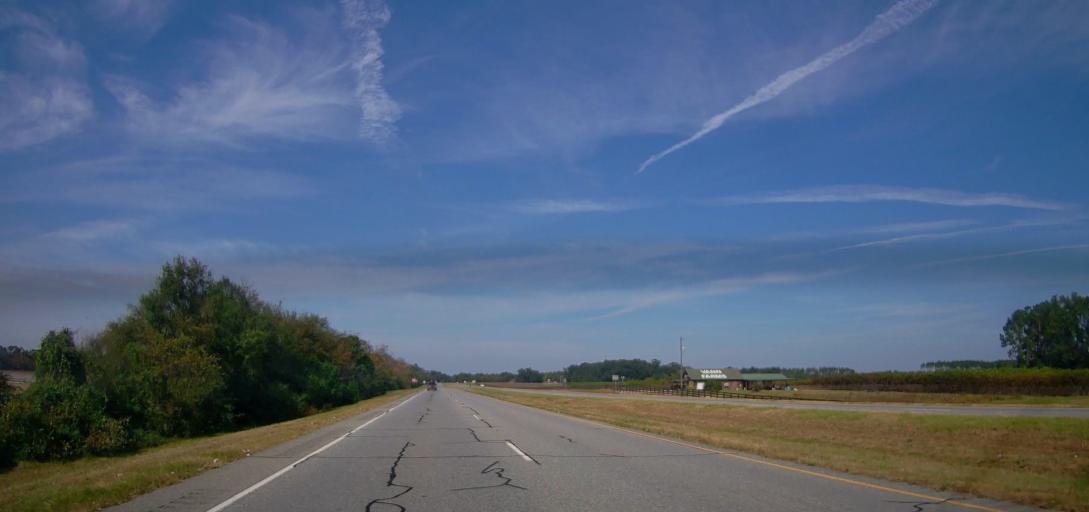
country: US
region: Georgia
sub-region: Mitchell County
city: Camilla
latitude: 31.3284
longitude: -84.1723
